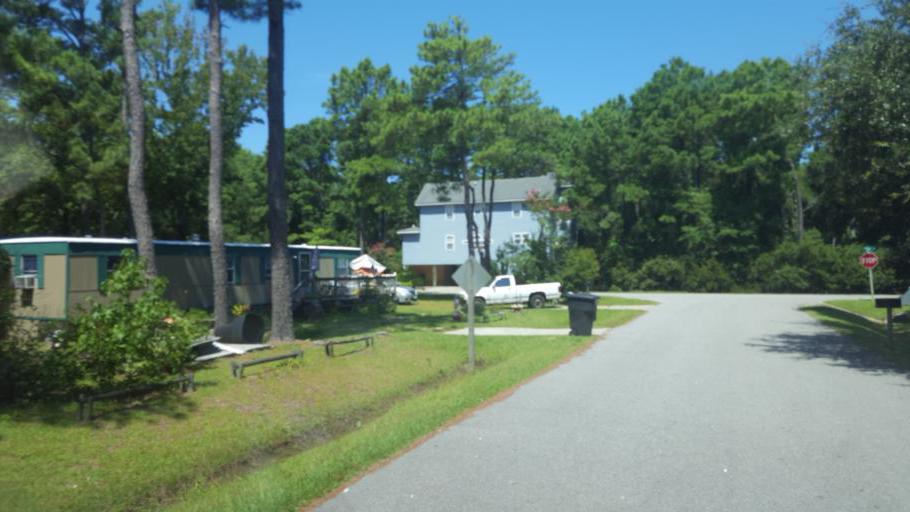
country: US
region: North Carolina
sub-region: Dare County
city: Kill Devil Hills
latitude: 35.9968
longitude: -75.6619
